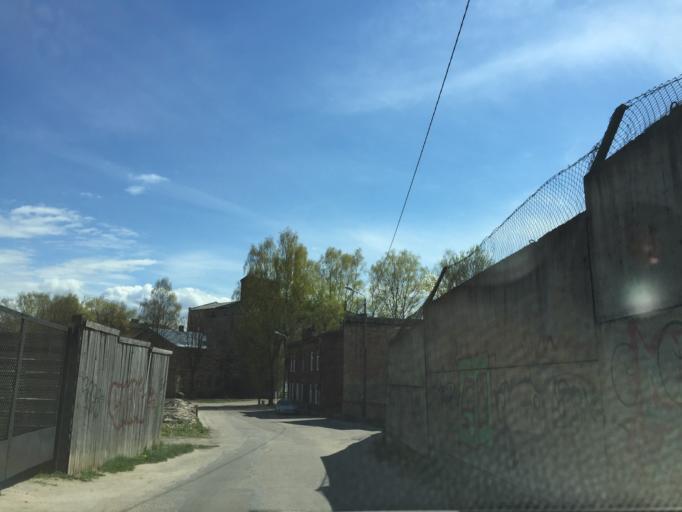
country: LV
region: Riga
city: Riga
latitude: 56.9268
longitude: 24.0961
